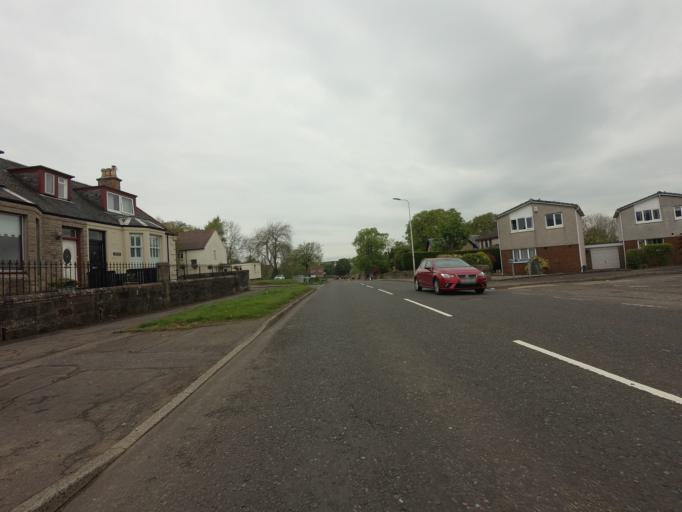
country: GB
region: Scotland
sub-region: Falkirk
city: Polmont
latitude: 55.9819
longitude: -3.7238
